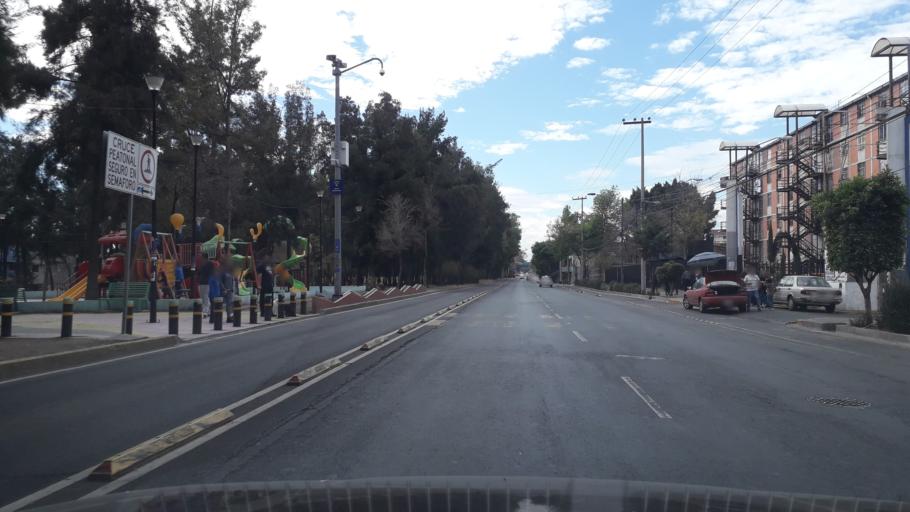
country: MX
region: Mexico City
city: Gustavo A. Madero
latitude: 19.4903
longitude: -99.0934
